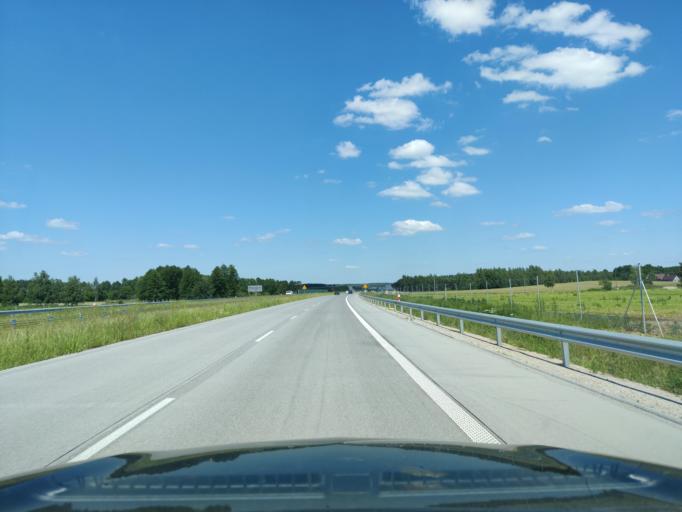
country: PL
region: Masovian Voivodeship
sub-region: Powiat mlawski
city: Strzegowo
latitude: 52.9570
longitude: 20.3056
